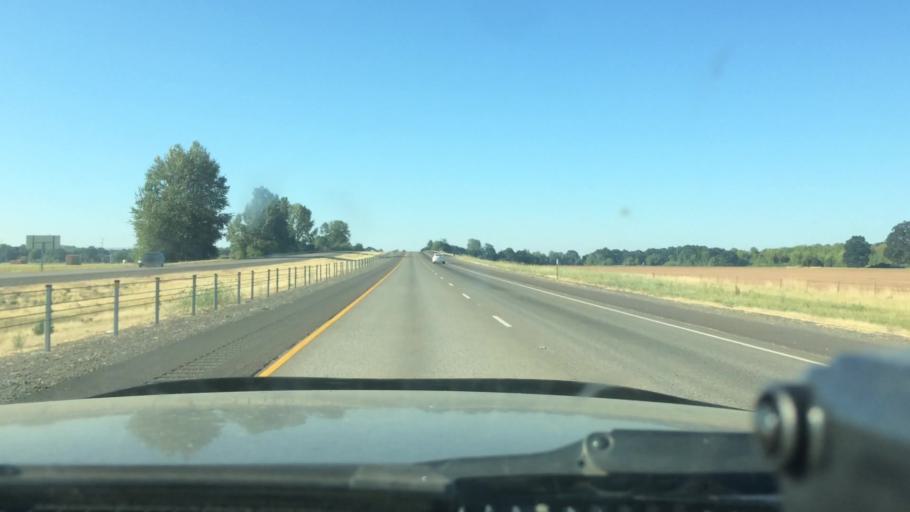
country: US
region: Oregon
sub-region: Linn County
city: Albany
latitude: 44.6012
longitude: -123.0622
